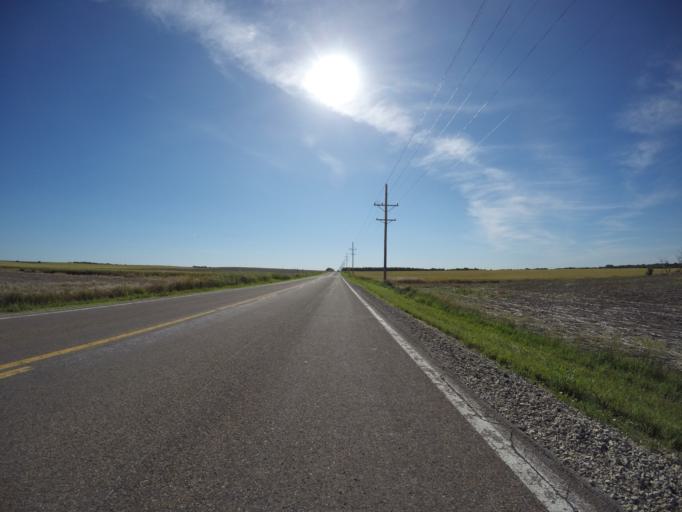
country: US
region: Kansas
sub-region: Mitchell County
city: Beloit
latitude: 39.6393
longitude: -97.9415
